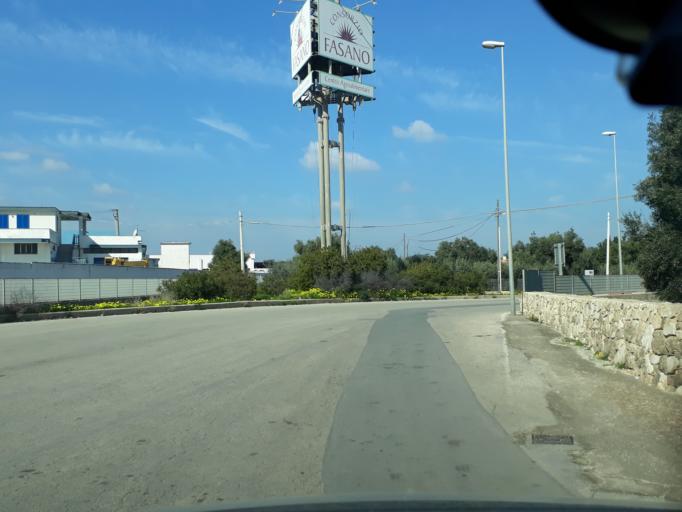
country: IT
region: Apulia
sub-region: Provincia di Brindisi
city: Fasano
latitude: 40.8263
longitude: 17.3835
